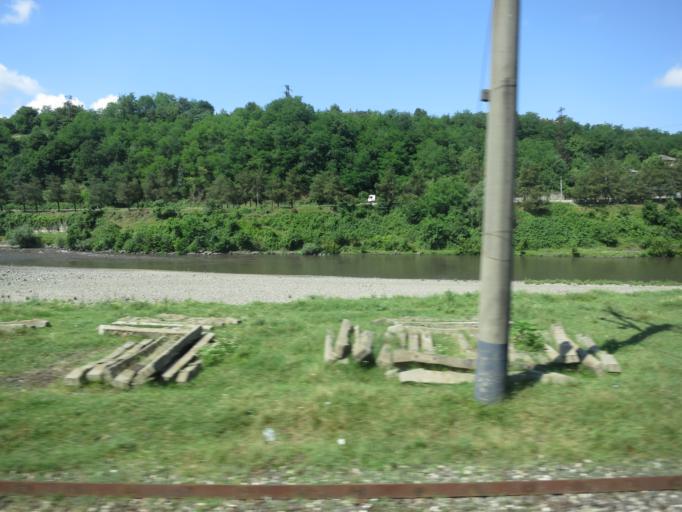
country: GE
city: Shorapani
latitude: 42.0990
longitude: 43.0760
